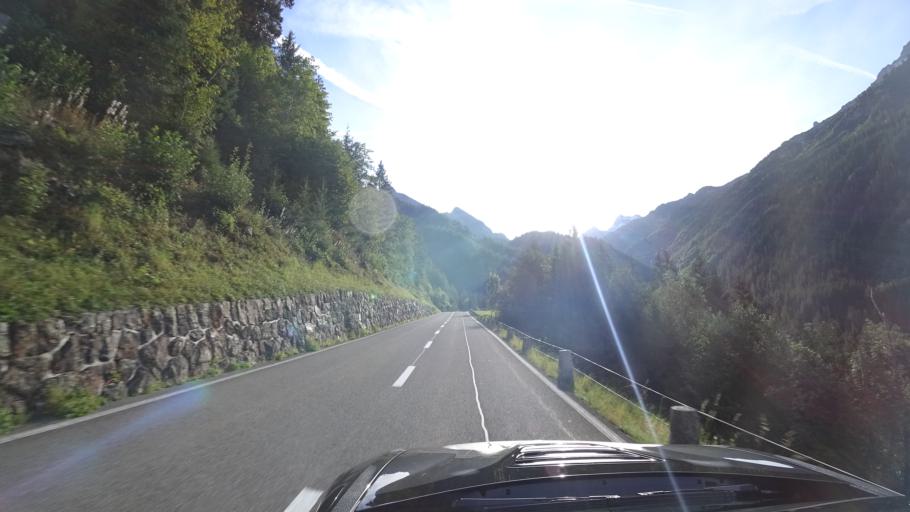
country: CH
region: Obwalden
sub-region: Obwalden
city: Engelberg
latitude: 46.7392
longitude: 8.3698
